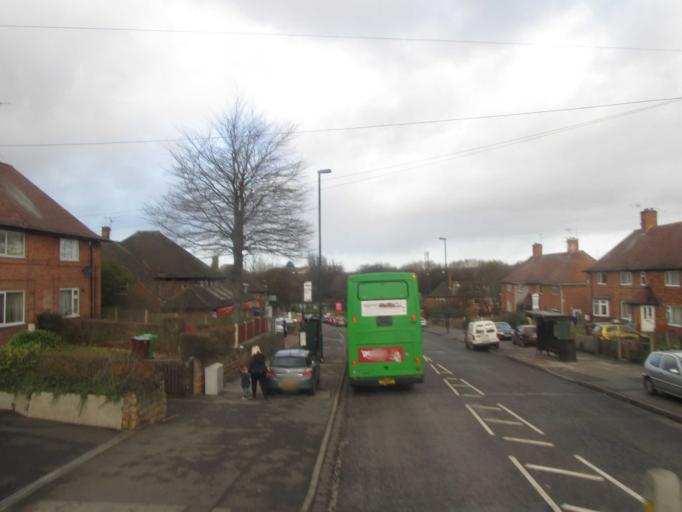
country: GB
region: England
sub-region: Nottinghamshire
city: Hucknall
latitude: 52.9851
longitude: -1.2043
